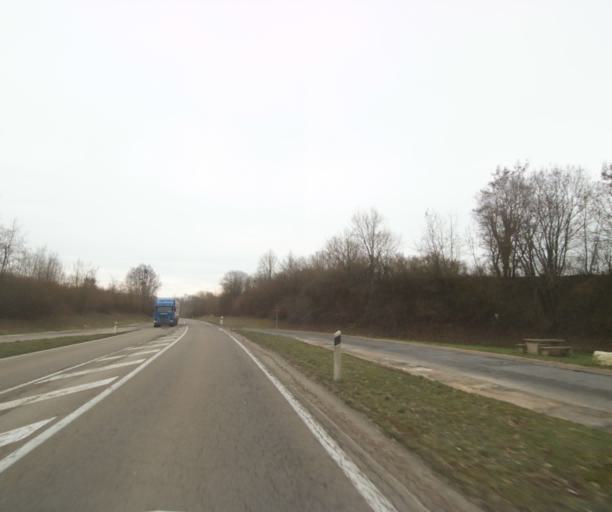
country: FR
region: Champagne-Ardenne
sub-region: Departement de la Haute-Marne
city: Bienville
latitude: 48.5804
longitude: 5.0302
